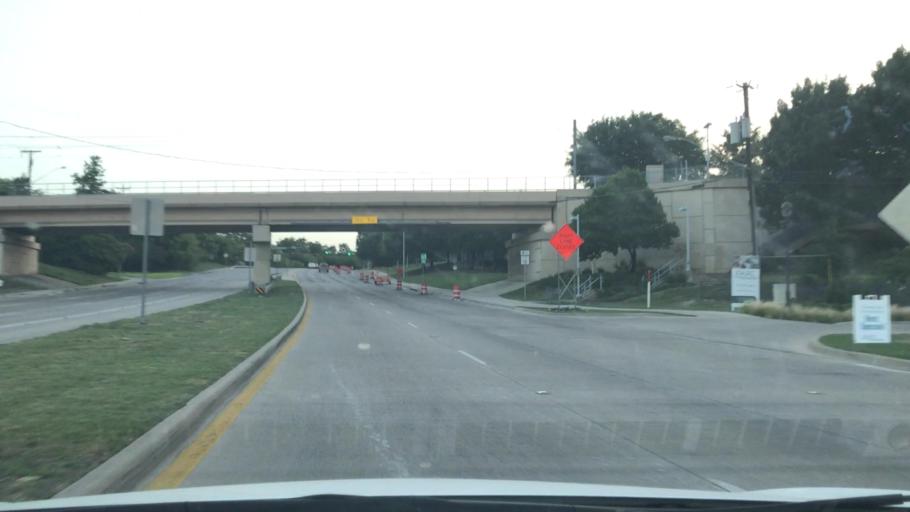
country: US
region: Texas
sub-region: Dallas County
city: Highland Park
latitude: 32.8554
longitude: -96.7319
